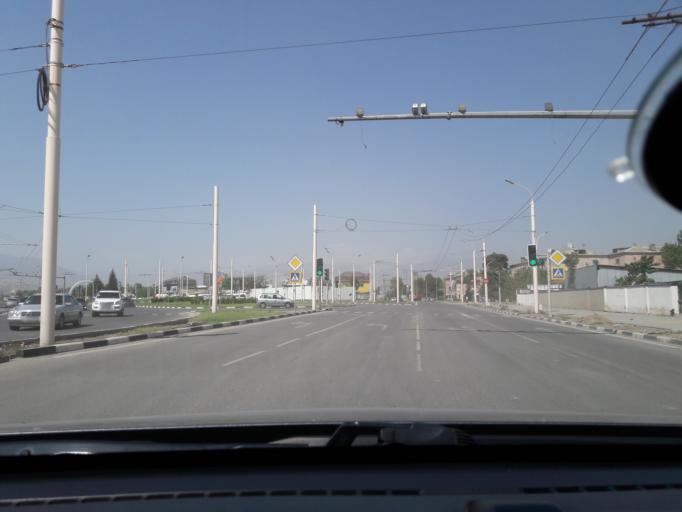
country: TJ
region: Dushanbe
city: Dushanbe
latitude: 38.5360
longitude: 68.7408
